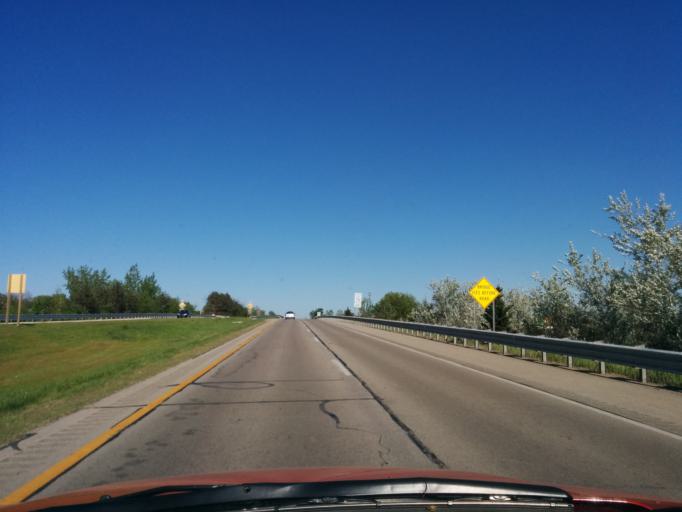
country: US
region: Michigan
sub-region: Midland County
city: Midland
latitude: 43.6113
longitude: -84.2142
